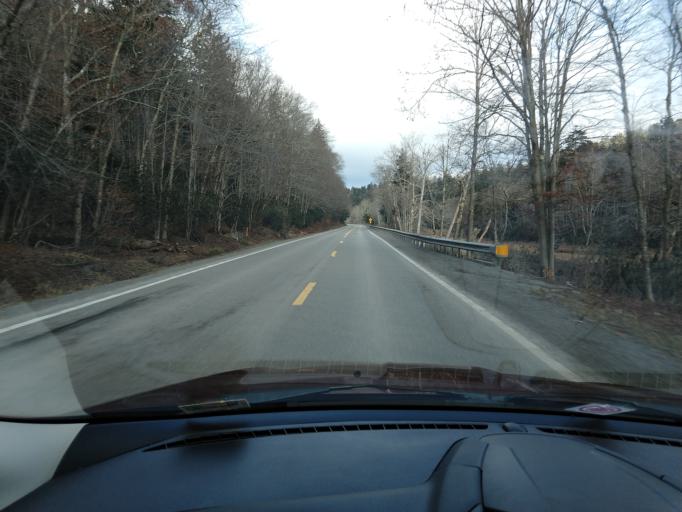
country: US
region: West Virginia
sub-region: Randolph County
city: Elkins
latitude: 38.6303
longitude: -79.8786
